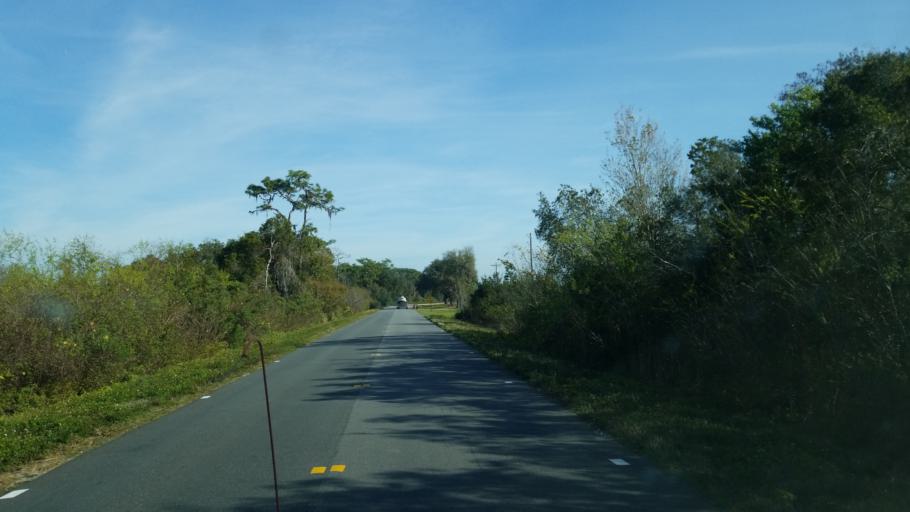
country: US
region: Florida
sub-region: Lake County
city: Clermont
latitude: 28.4314
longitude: -81.8080
